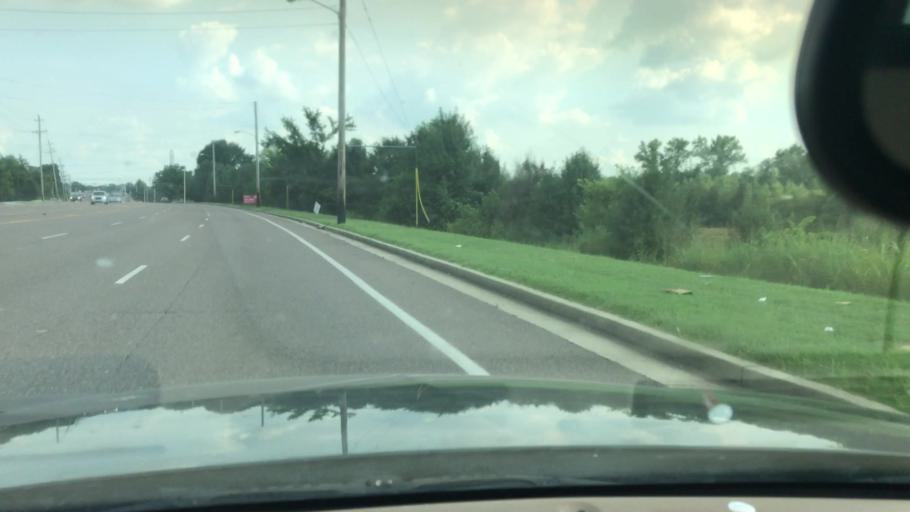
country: US
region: Tennessee
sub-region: Shelby County
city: Bartlett
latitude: 35.1925
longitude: -89.8151
